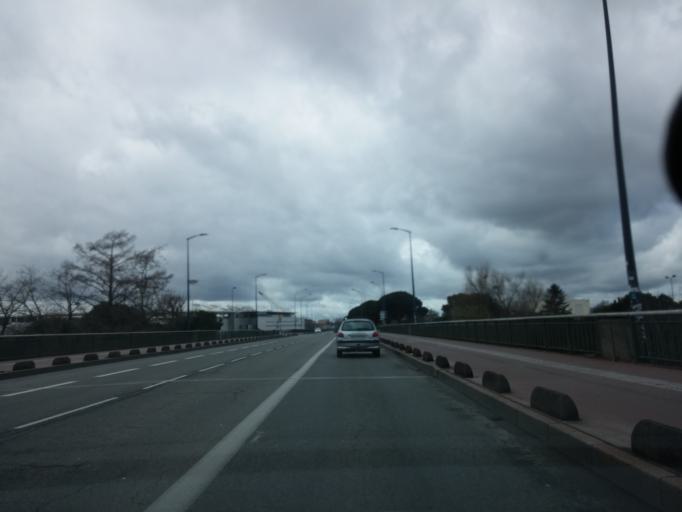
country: FR
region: Midi-Pyrenees
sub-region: Departement de la Haute-Garonne
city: Toulouse
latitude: 43.5842
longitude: 1.4388
